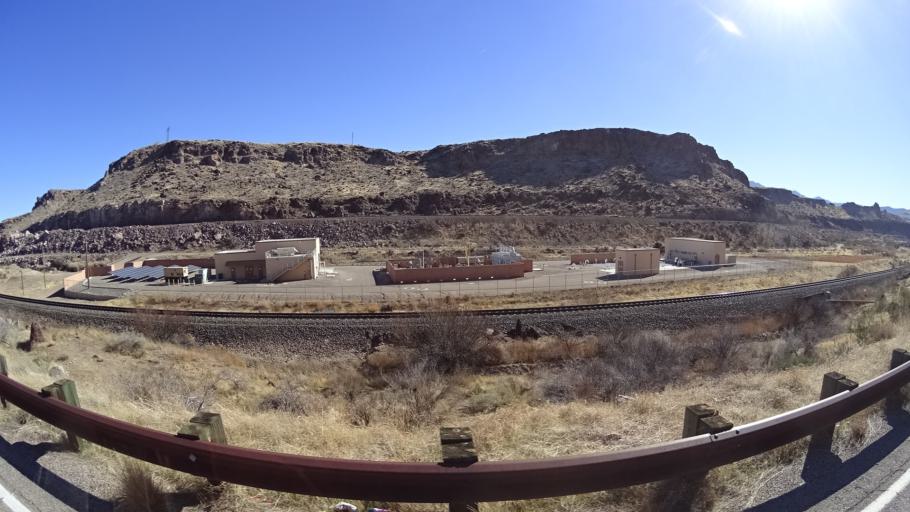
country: US
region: Arizona
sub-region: Mohave County
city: Kingman
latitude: 35.1764
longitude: -114.0645
